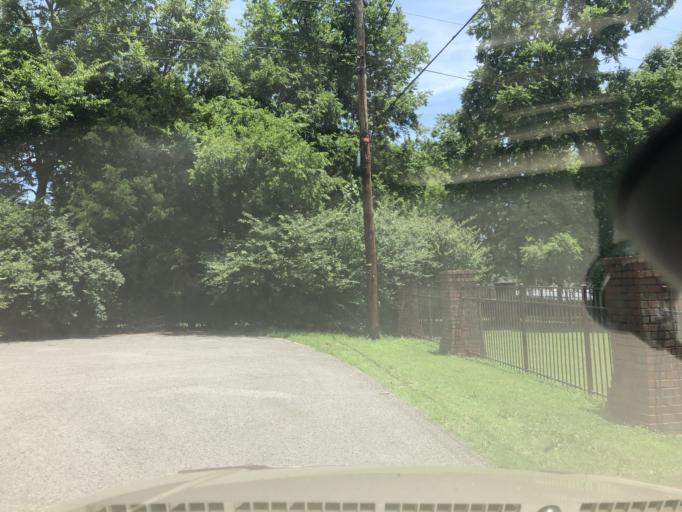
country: US
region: Tennessee
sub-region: Davidson County
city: Lakewood
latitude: 36.2480
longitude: -86.6954
